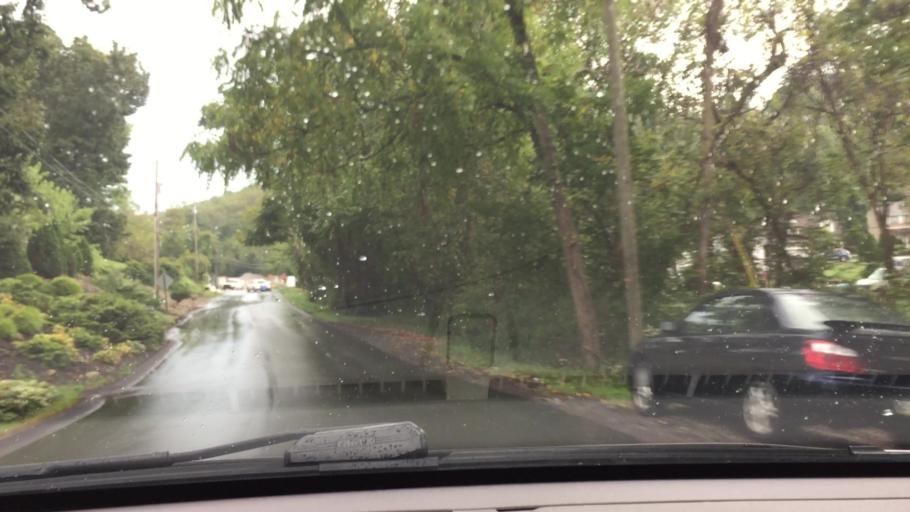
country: US
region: Pennsylvania
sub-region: Washington County
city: Canonsburg
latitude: 40.2763
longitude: -80.1925
